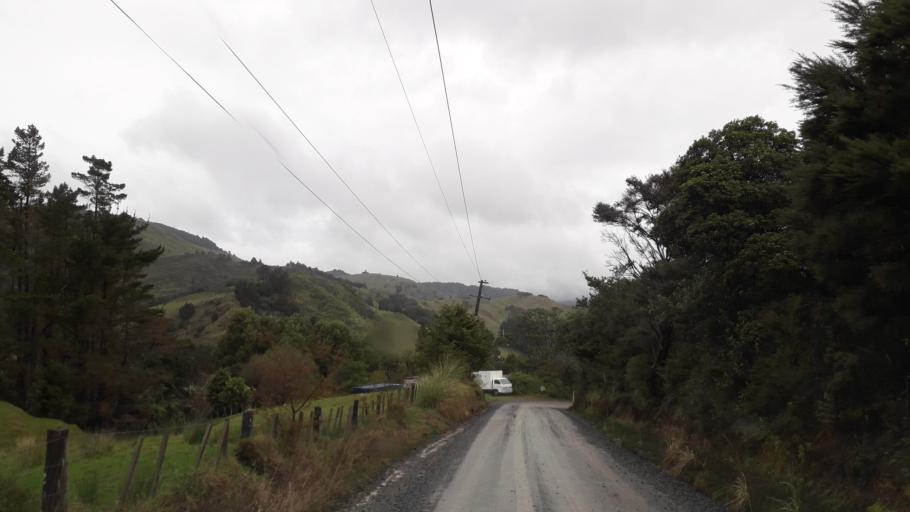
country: NZ
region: Northland
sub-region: Far North District
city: Kerikeri
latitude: -35.1243
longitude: 173.7462
